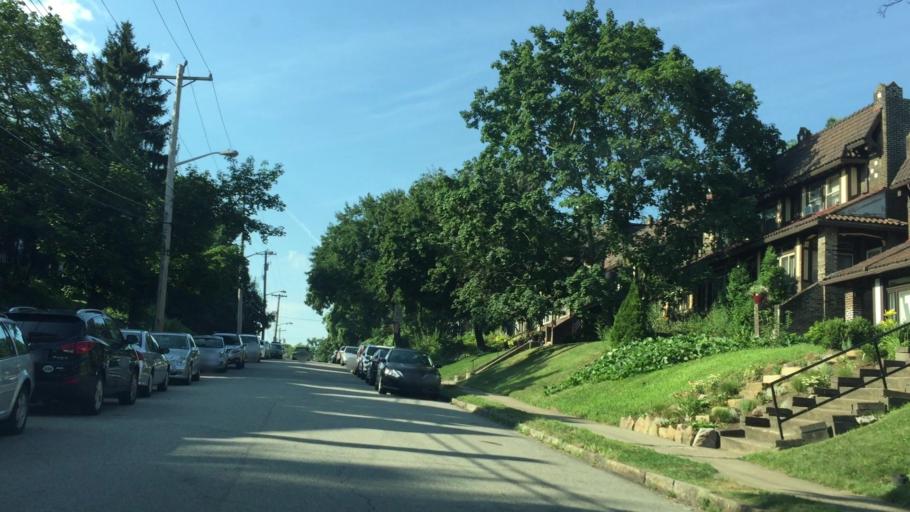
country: US
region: Pennsylvania
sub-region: Allegheny County
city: Homestead
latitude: 40.4401
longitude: -79.9180
